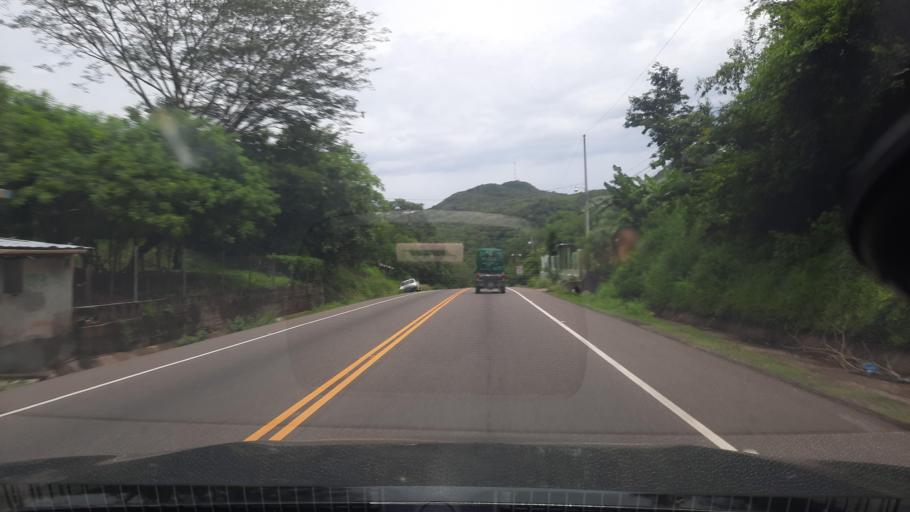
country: HN
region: Valle
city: Goascoran
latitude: 13.5667
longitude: -87.6715
